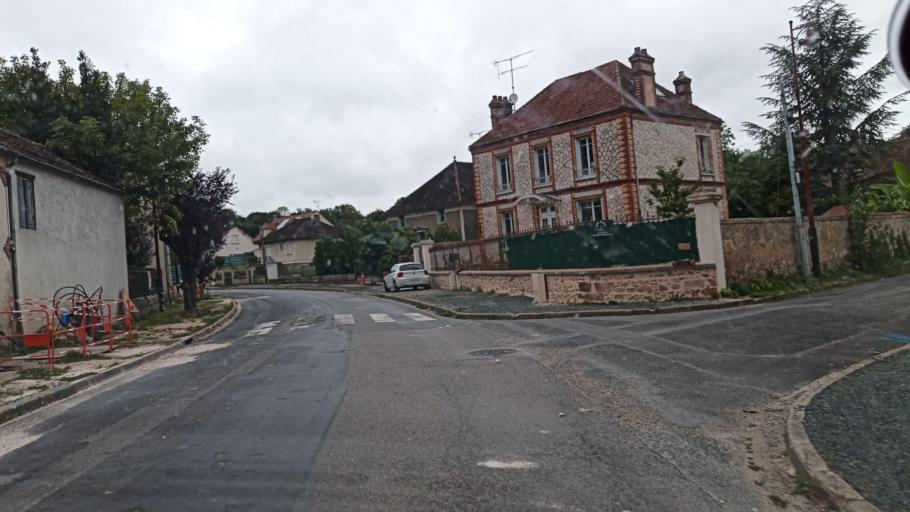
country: FR
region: Ile-de-France
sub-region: Departement de Seine-et-Marne
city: Voulx
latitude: 48.2839
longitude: 2.9687
